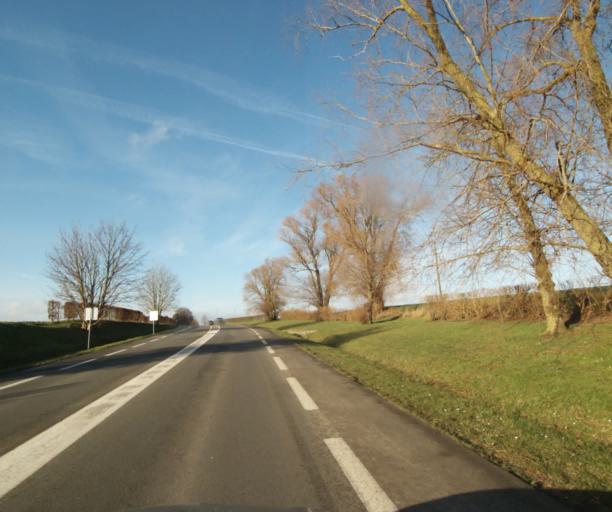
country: FR
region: Nord-Pas-de-Calais
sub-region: Departement du Nord
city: Preseau
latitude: 50.3169
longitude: 3.5702
